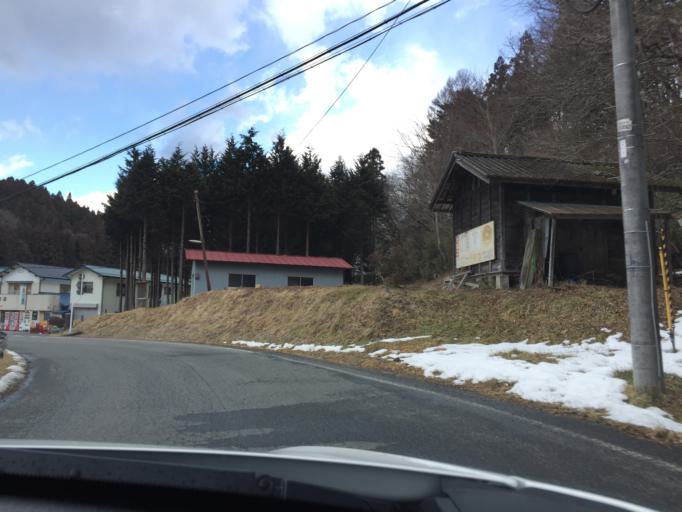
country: JP
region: Fukushima
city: Iwaki
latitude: 37.2434
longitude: 140.7277
